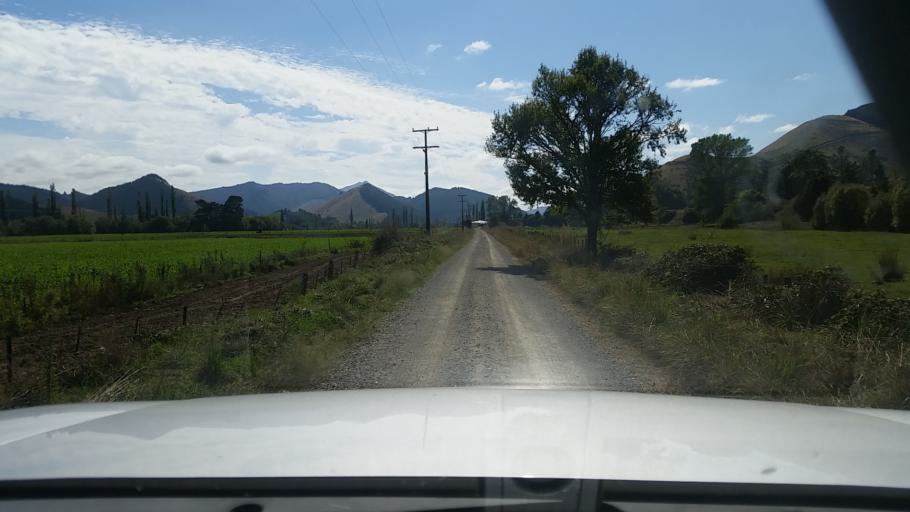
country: NZ
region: Nelson
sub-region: Nelson City
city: Nelson
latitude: -41.2533
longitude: 173.5827
